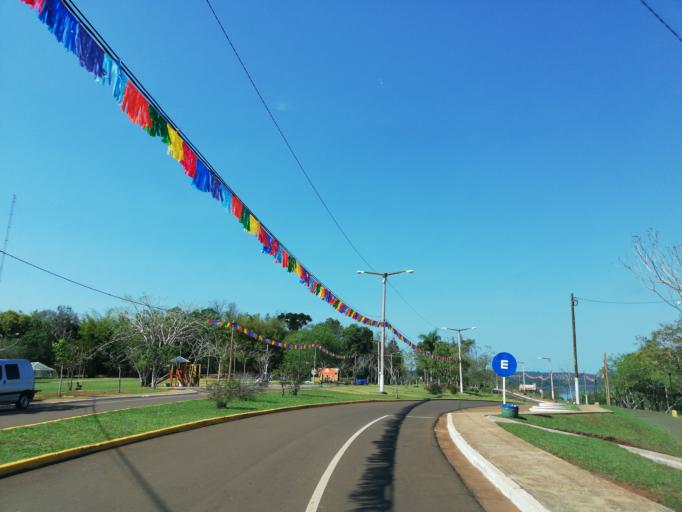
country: AR
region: Misiones
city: Puerto Eldorado
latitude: -26.4114
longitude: -54.6932
